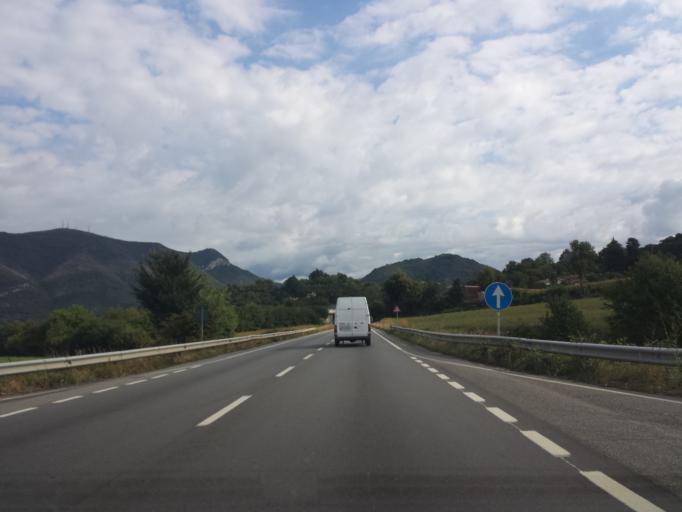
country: IT
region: Lombardy
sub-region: Provincia di Brescia
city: Gavardo-Sopraponte
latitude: 45.5797
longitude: 10.4474
